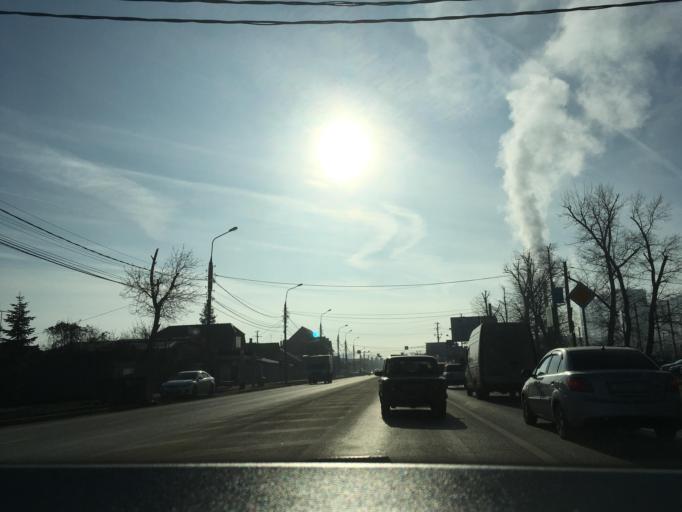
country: RU
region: Krasnodarskiy
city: Krasnodar
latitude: 45.0961
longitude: 39.0135
